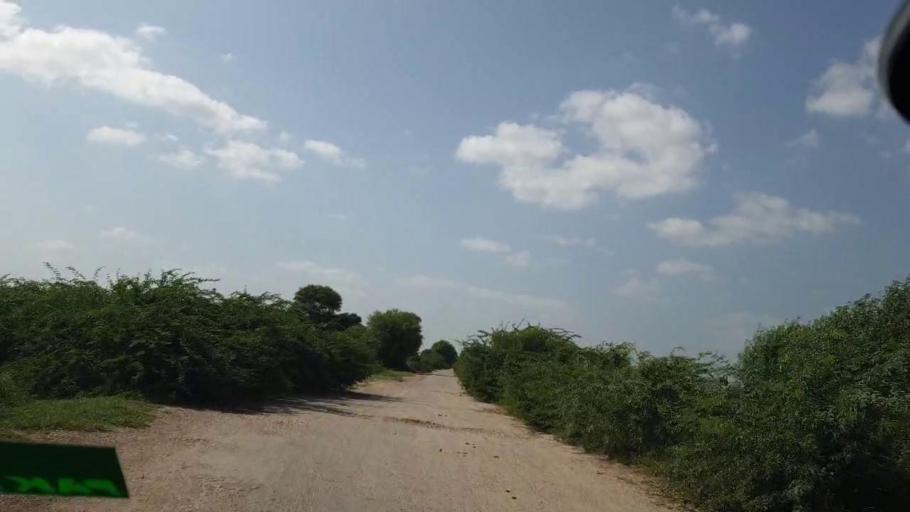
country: PK
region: Sindh
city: Naukot
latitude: 24.6527
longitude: 69.2161
